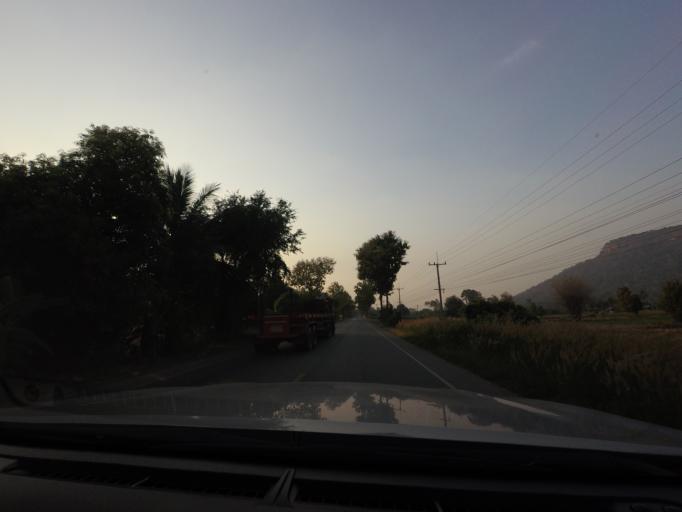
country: TH
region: Phitsanulok
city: Wang Thong
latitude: 16.7110
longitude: 100.4800
